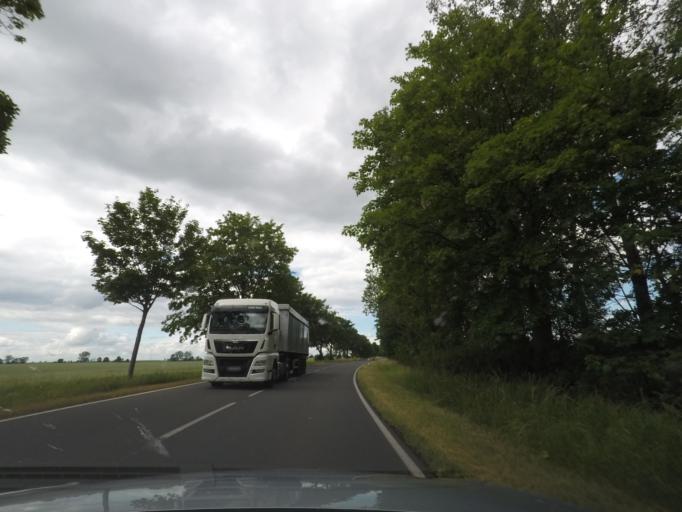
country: DE
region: Saxony-Anhalt
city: Ausleben
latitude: 52.0807
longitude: 11.0769
